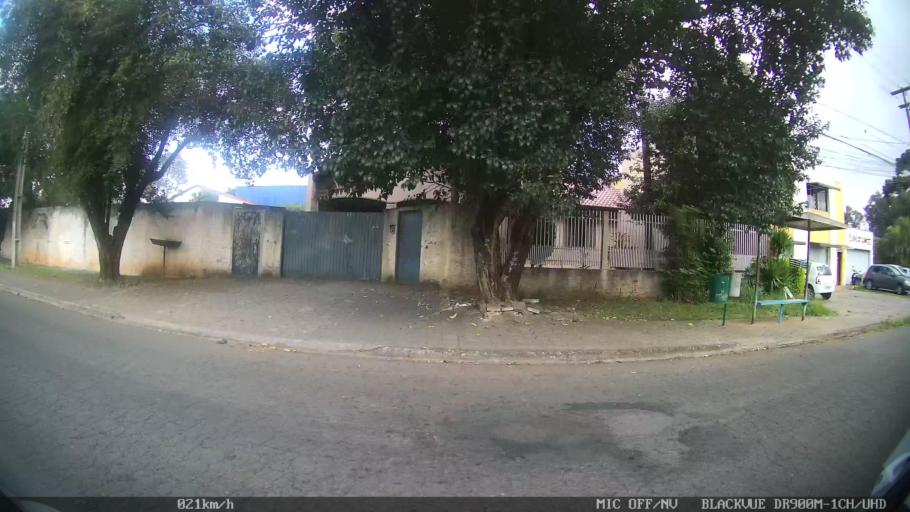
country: BR
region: Parana
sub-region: Pinhais
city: Pinhais
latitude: -25.4241
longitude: -49.1890
